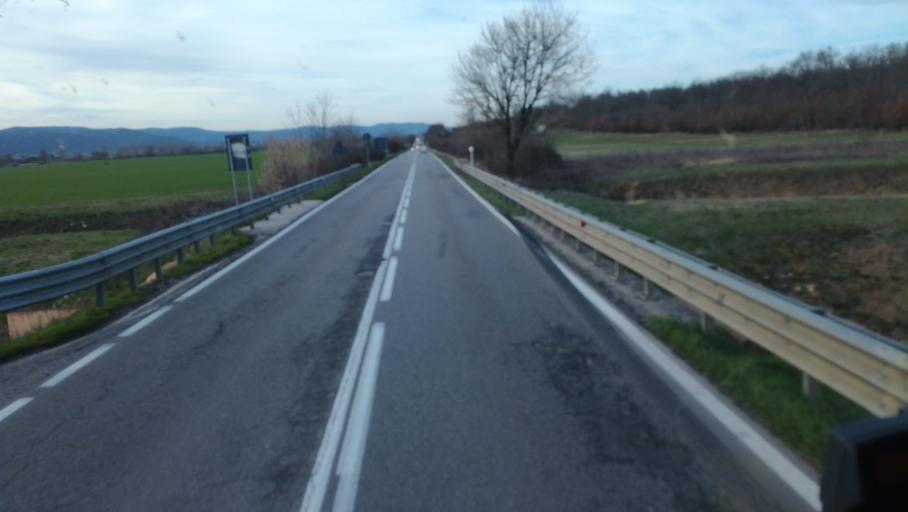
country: IT
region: Tuscany
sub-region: Provincia di Siena
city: Rosia
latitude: 43.2108
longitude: 11.2786
